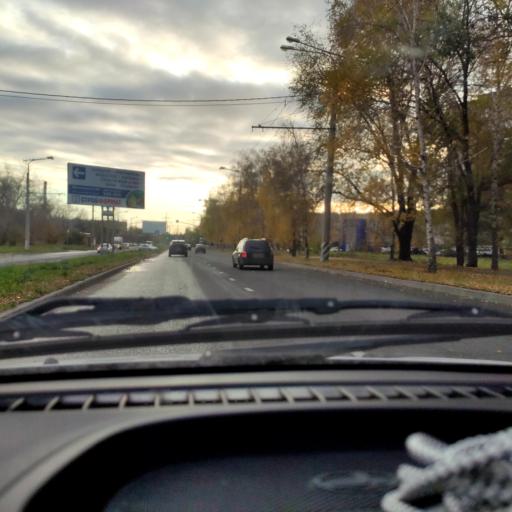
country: RU
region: Samara
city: Tol'yatti
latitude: 53.5136
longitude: 49.4485
